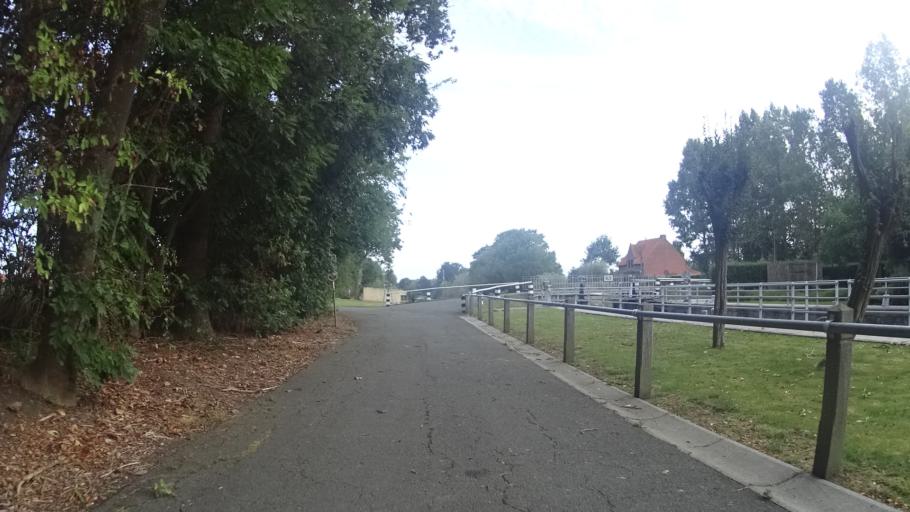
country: BE
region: Flanders
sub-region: Provincie West-Vlaanderen
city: Ieper
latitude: 50.9098
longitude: 2.8498
